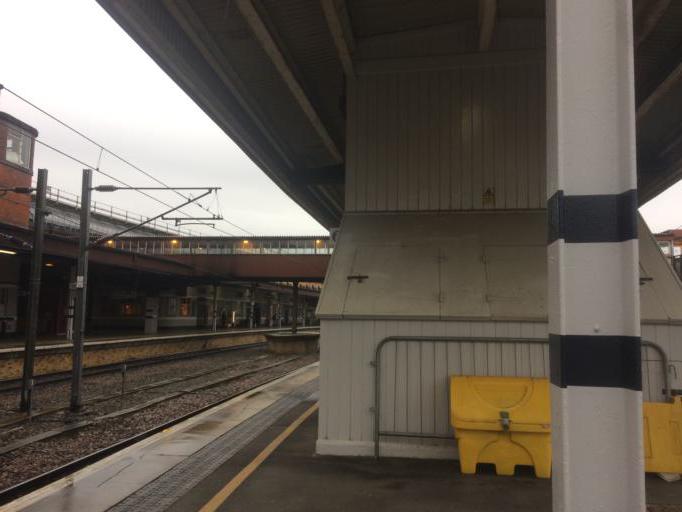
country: GB
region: England
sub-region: City of York
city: York
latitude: 53.9586
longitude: -1.0940
